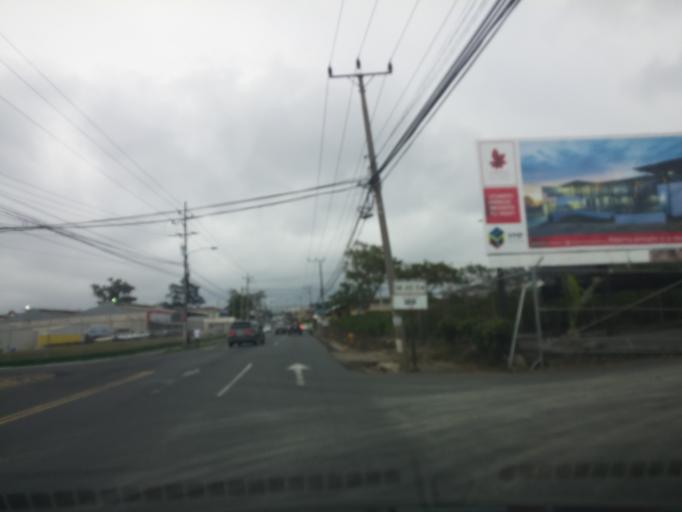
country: CR
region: Heredia
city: Llorente
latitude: 9.9827
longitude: -84.1487
